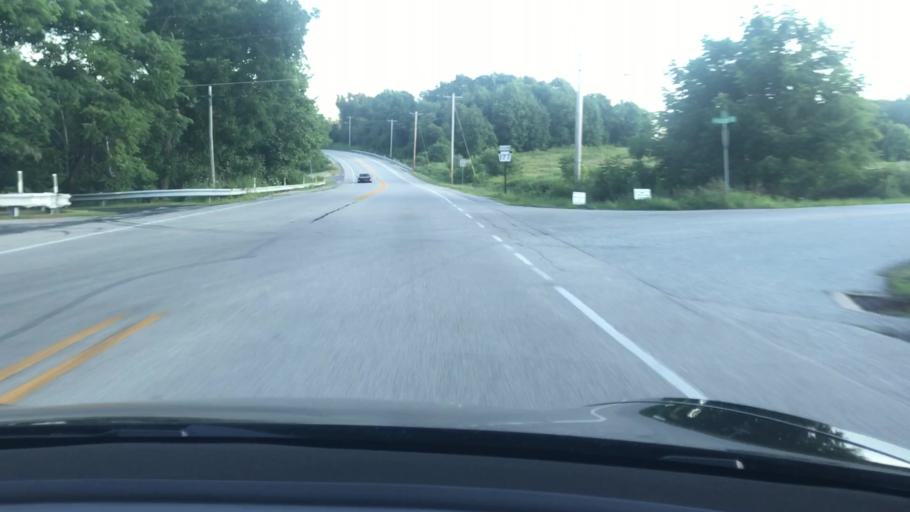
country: US
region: Pennsylvania
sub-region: York County
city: Valley Green
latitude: 40.1219
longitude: -76.8678
